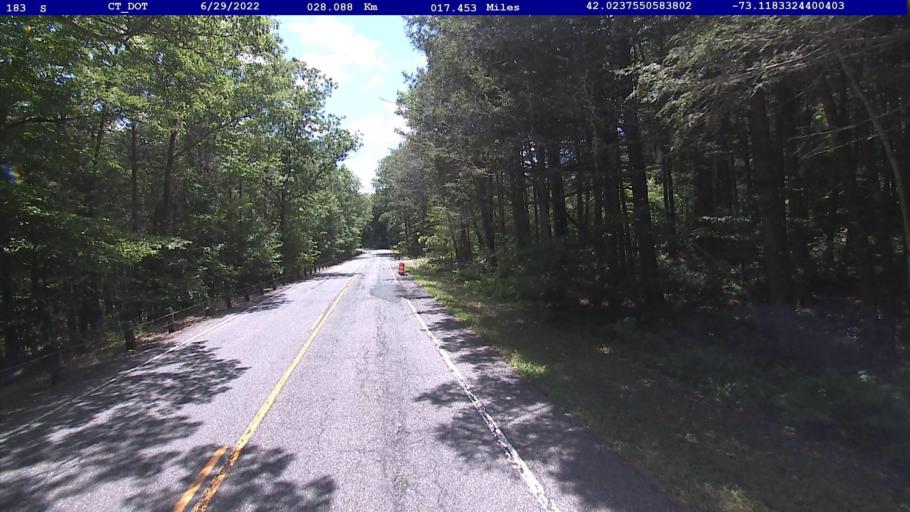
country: US
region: Connecticut
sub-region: Litchfield County
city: Winsted
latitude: 42.0237
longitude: -73.1183
